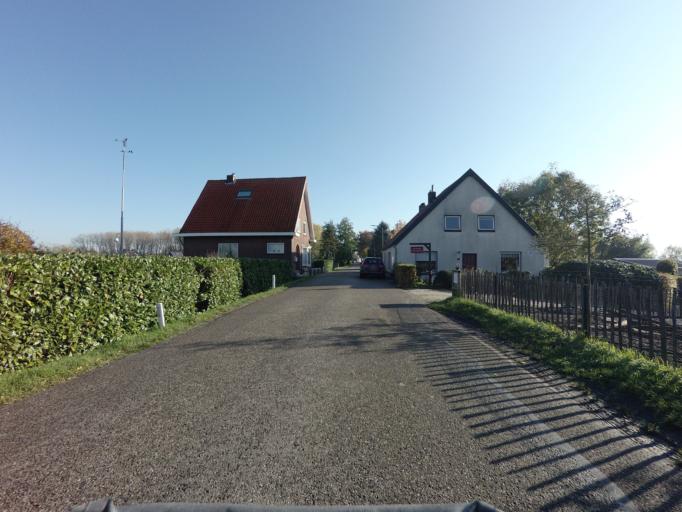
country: NL
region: North Brabant
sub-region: Gemeente Woudrichem
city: Almkerk
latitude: 51.7327
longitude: 4.9537
